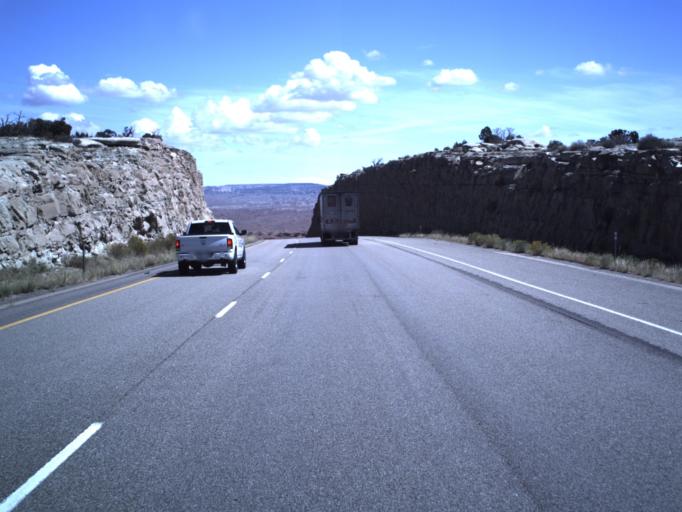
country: US
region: Utah
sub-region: Emery County
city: Ferron
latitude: 38.8302
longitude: -111.1165
